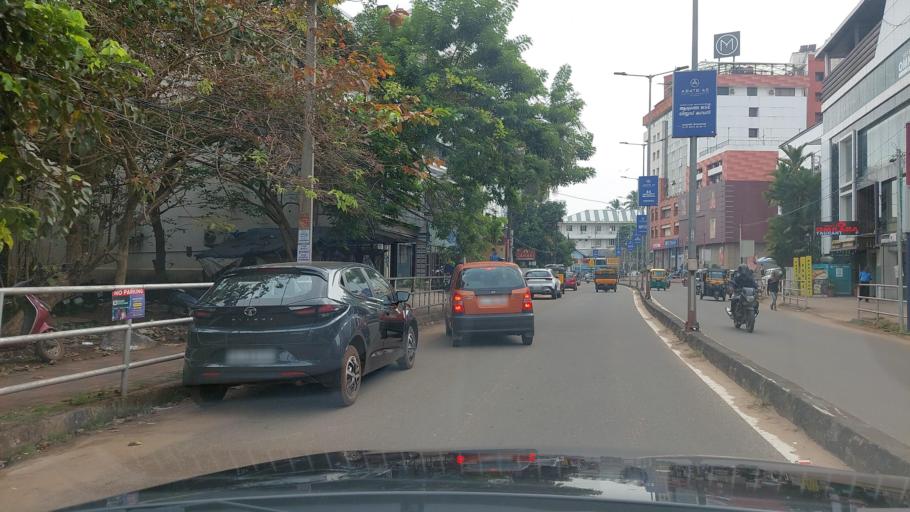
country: IN
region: Kerala
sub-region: Kozhikode
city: Kozhikode
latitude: 11.2541
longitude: 75.7869
